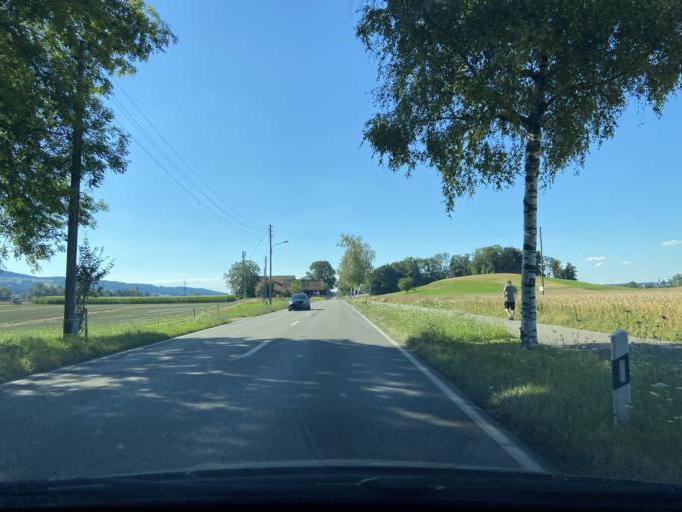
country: CH
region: Zurich
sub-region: Bezirk Uster
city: Monchaltorf
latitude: 47.3175
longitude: 8.7191
